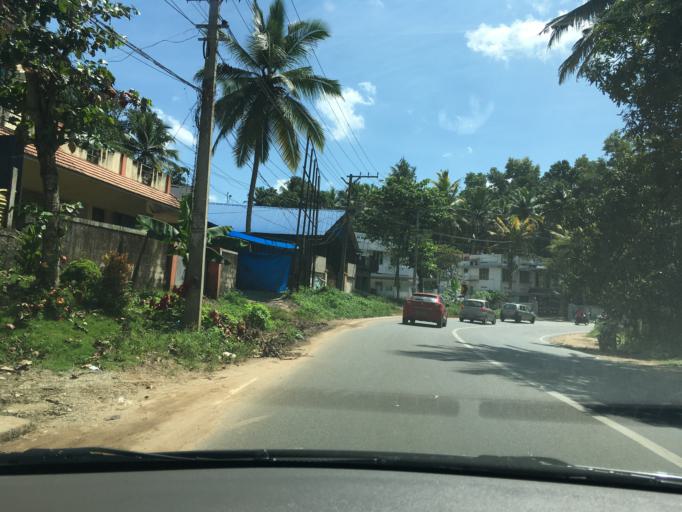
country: IN
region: Kerala
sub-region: Thiruvananthapuram
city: Nedumangad
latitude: 8.5727
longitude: 76.9950
